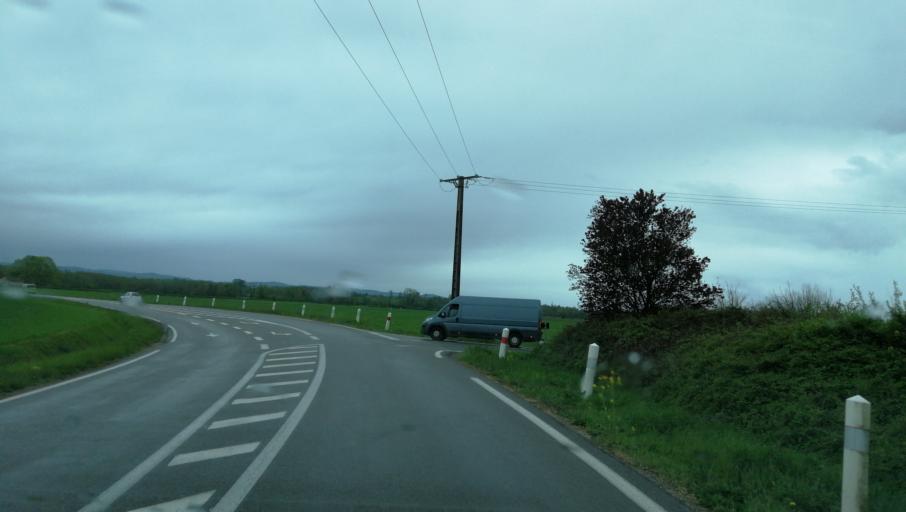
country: FR
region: Franche-Comte
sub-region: Departement du Jura
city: Bletterans
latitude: 46.7319
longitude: 5.4693
